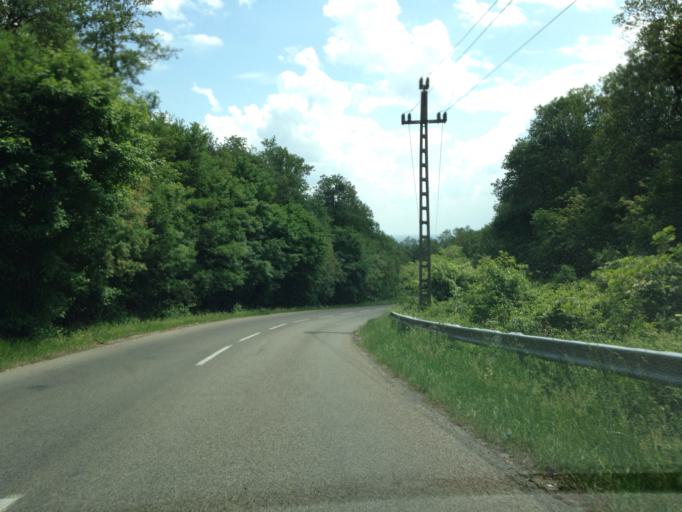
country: HU
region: Pest
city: Nagykovacsi
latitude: 47.7063
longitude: 19.0168
